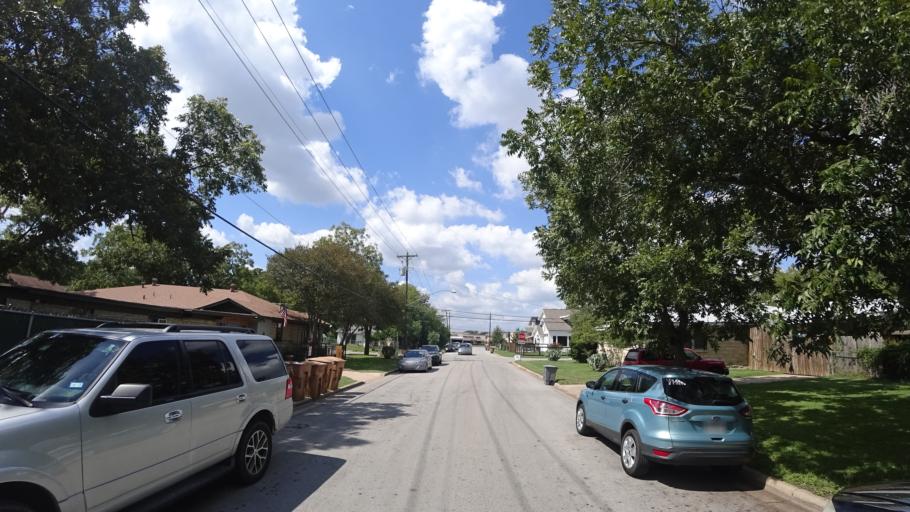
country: US
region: Texas
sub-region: Williamson County
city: Jollyville
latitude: 30.3658
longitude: -97.7267
